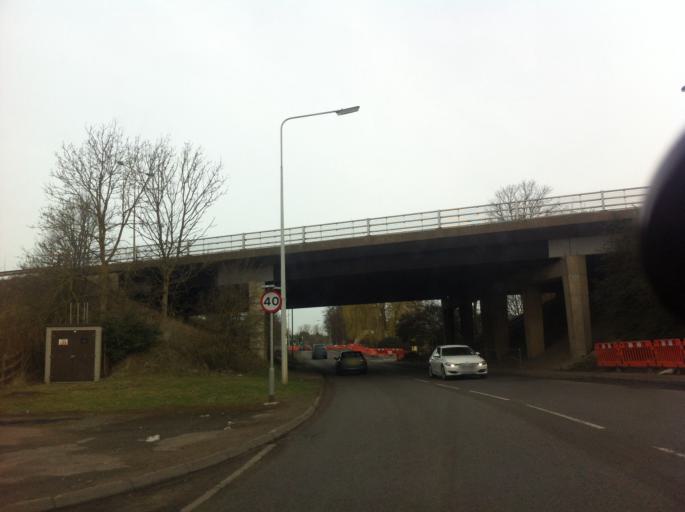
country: GB
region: England
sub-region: Northamptonshire
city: Wellingborough
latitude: 52.2882
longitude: -0.6792
